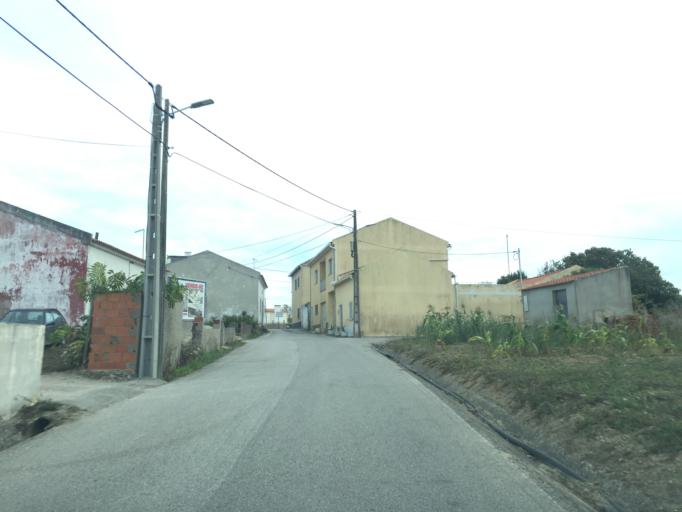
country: PT
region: Leiria
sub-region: Peniche
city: Atouguia da Baleia
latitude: 39.3422
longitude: -9.2949
